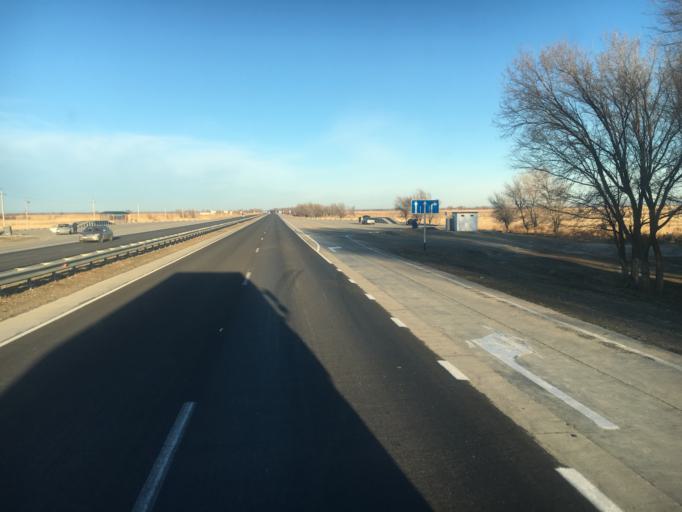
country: KZ
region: Ongtustik Qazaqstan
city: Bayaldyr
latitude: 43.0887
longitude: 68.6426
